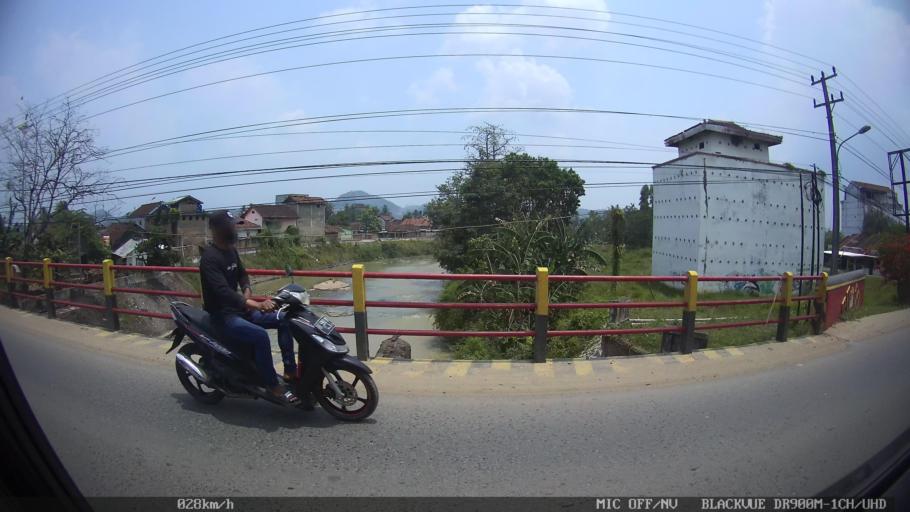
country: ID
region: Lampung
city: Pringsewu
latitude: -5.3629
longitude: 105.0021
